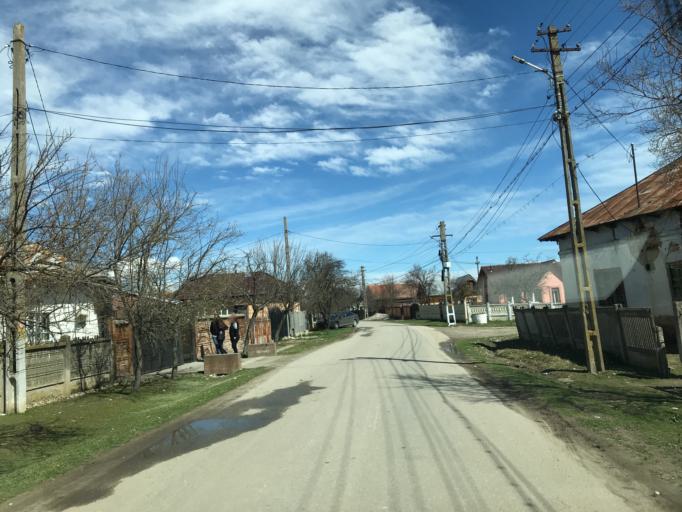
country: RO
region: Olt
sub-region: Comuna Osica de Sus
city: Osica de Sus
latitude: 44.2525
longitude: 24.3148
